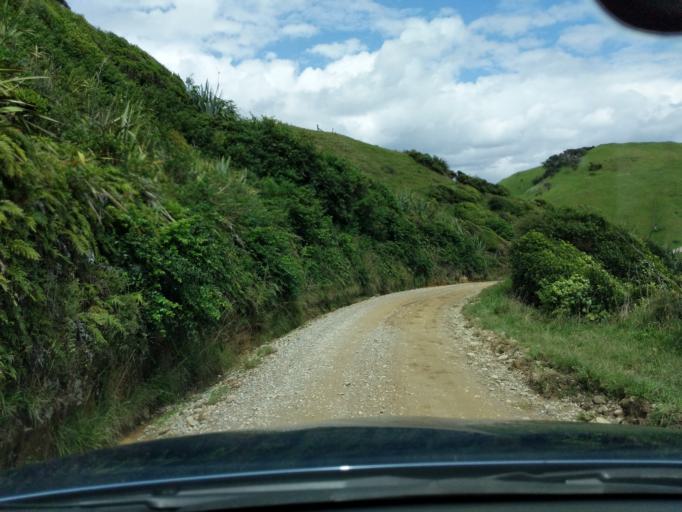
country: NZ
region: Tasman
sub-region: Tasman District
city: Takaka
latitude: -40.6700
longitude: 172.3996
